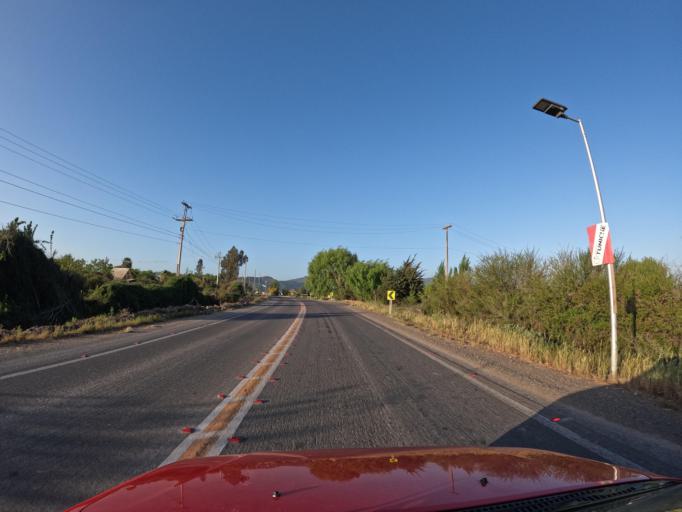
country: CL
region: O'Higgins
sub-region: Provincia de Cachapoal
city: San Vicente
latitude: -34.2939
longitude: -71.3690
